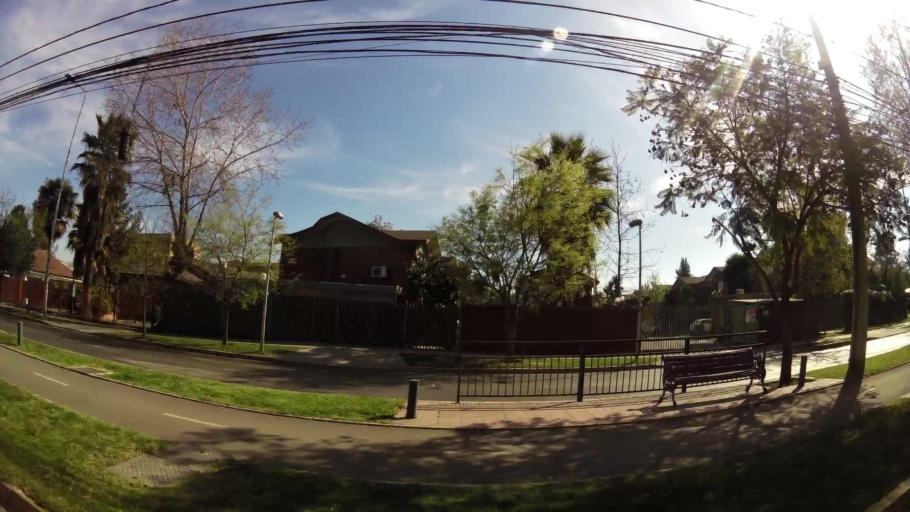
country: CL
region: Santiago Metropolitan
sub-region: Provincia de Santiago
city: Villa Presidente Frei, Nunoa, Santiago, Chile
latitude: -33.4512
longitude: -70.5504
